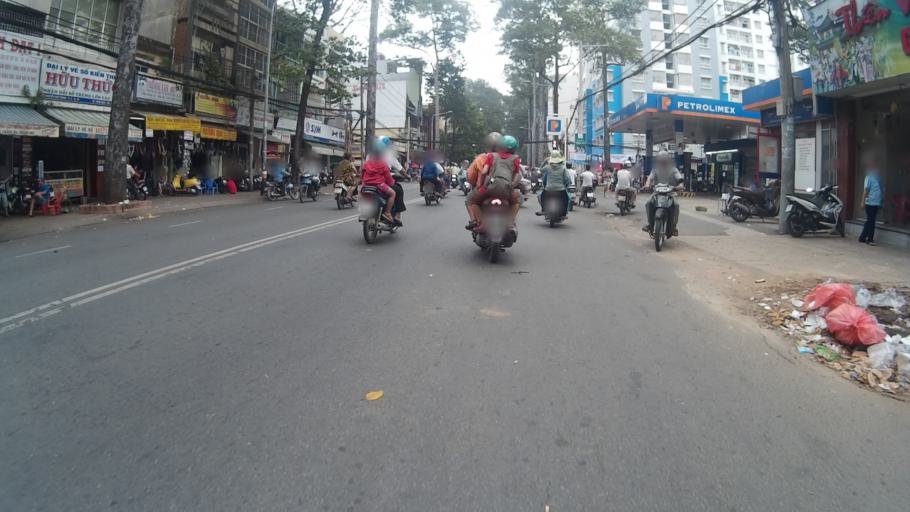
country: VN
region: Ho Chi Minh City
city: Quan Nam
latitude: 10.7590
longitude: 106.6648
